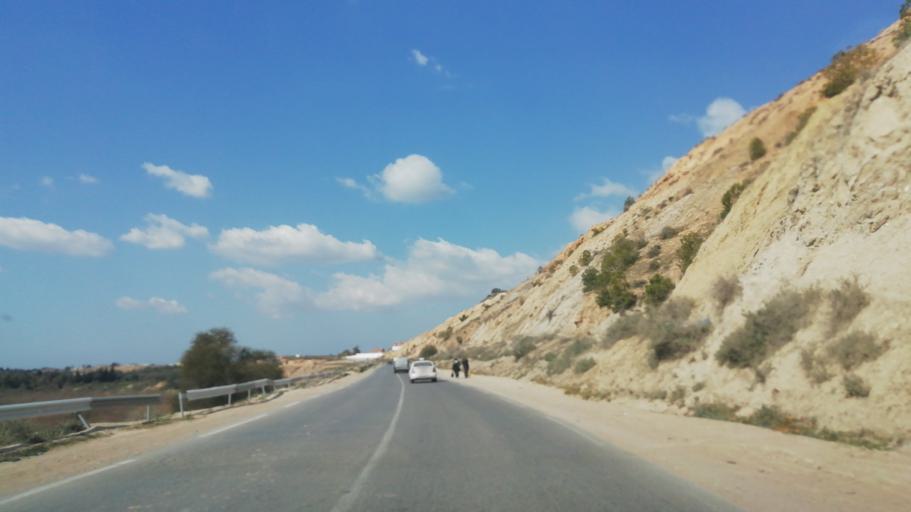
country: DZ
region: Mascara
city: Mascara
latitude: 35.5668
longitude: 0.0718
